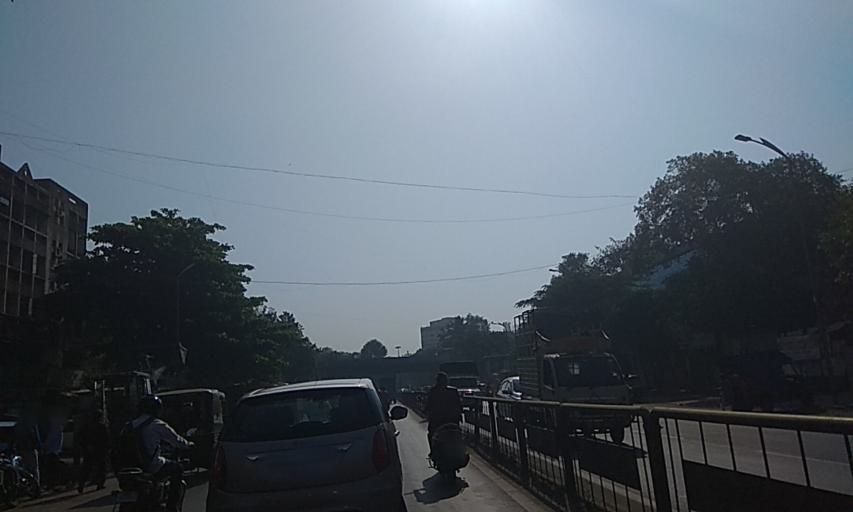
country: IN
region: Maharashtra
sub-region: Pune Division
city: Pune
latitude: 18.5003
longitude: 73.8494
